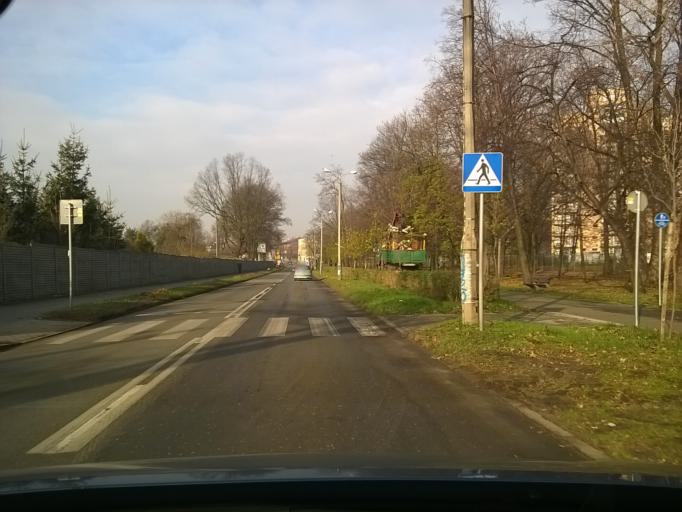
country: PL
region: Silesian Voivodeship
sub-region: Chorzow
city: Chorzow
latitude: 50.2837
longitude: 18.9523
